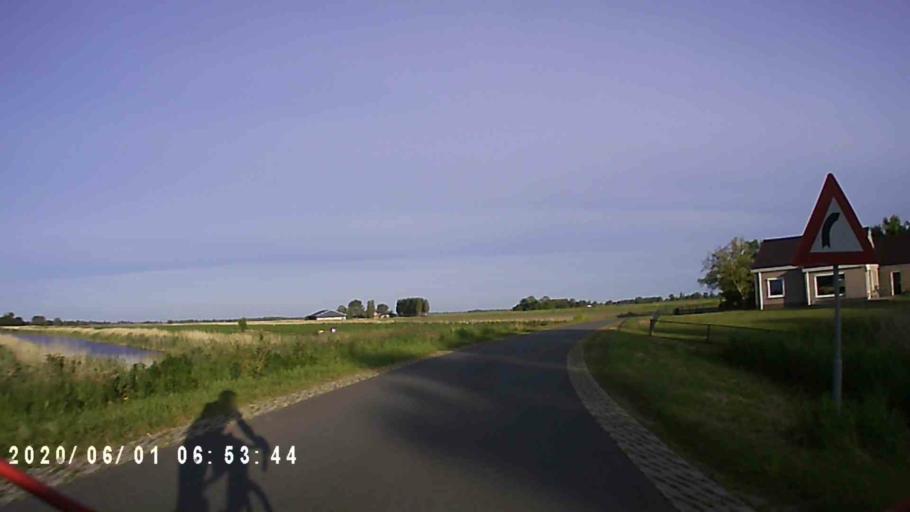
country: NL
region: Friesland
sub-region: Gemeente Kollumerland en Nieuwkruisland
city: Kollum
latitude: 53.3117
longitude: 6.1271
